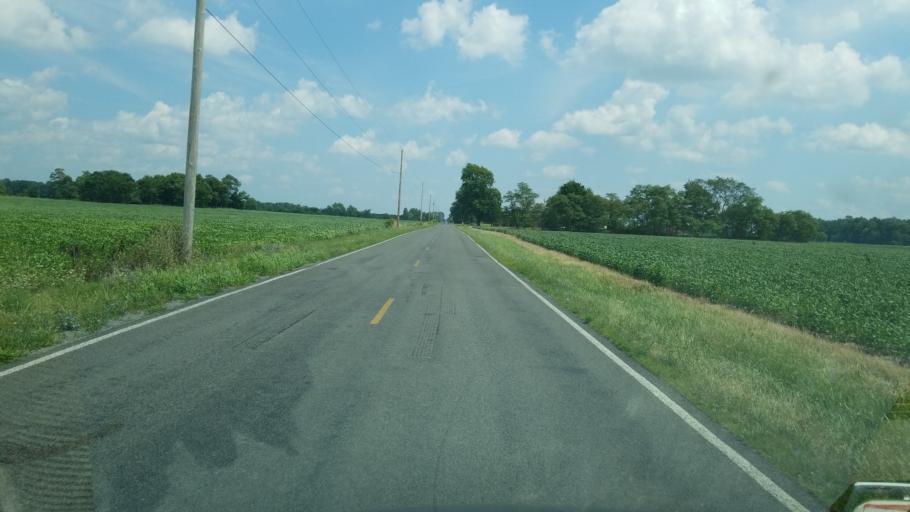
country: US
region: Ohio
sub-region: Hancock County
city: Arlington
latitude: 40.9071
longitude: -83.7161
